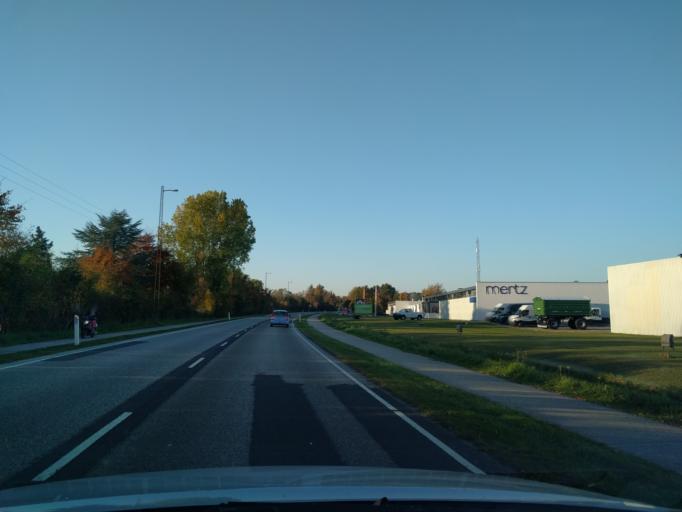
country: DK
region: Zealand
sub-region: Guldborgsund Kommune
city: Nykobing Falster
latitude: 54.7553
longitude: 11.8955
